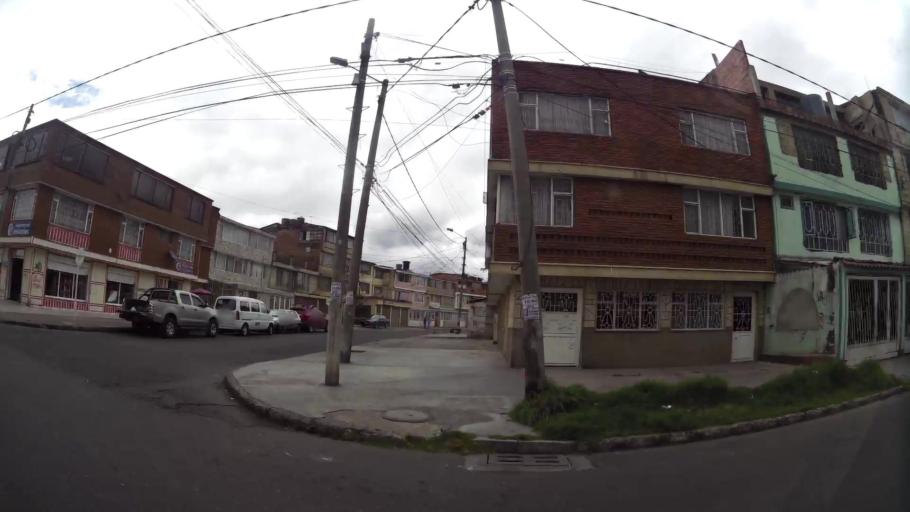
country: CO
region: Bogota D.C.
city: Bogota
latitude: 4.6201
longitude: -74.1091
